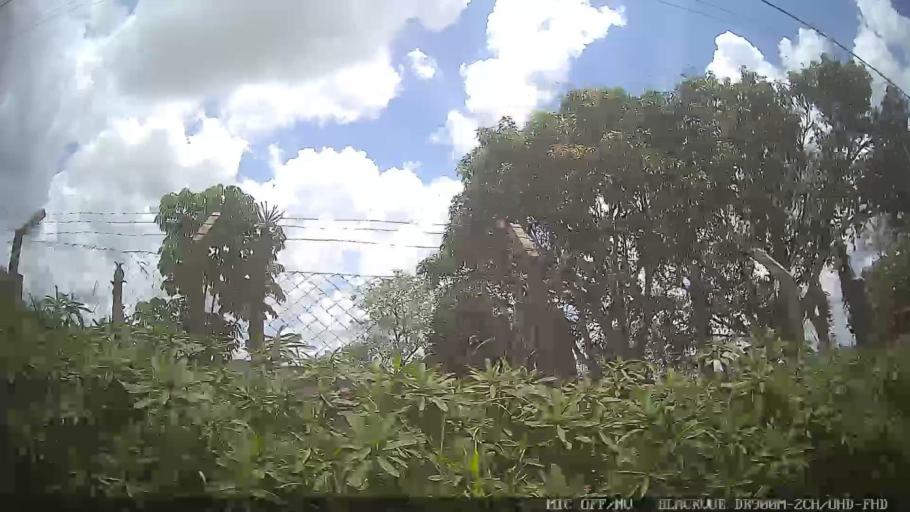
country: BR
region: Sao Paulo
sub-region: Braganca Paulista
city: Braganca Paulista
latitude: -23.0326
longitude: -46.5259
